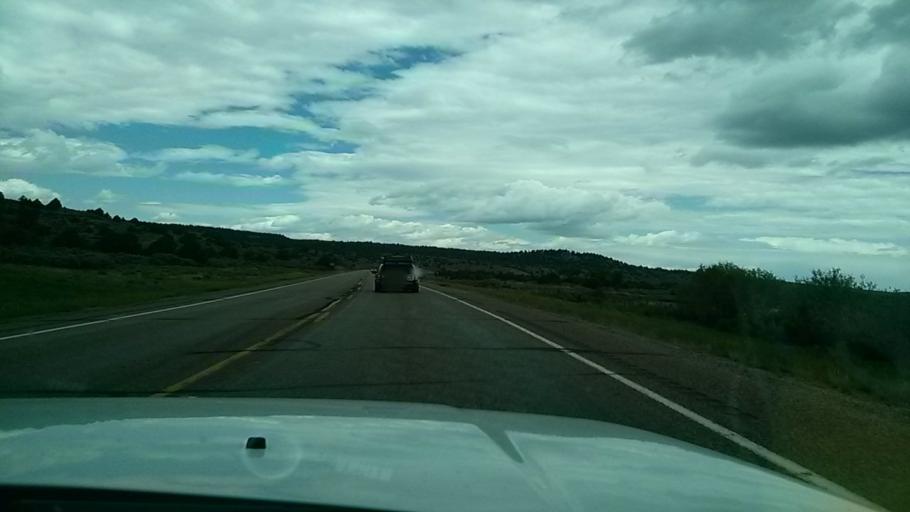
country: US
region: Utah
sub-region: Garfield County
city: Panguitch
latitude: 37.6832
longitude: -112.3989
